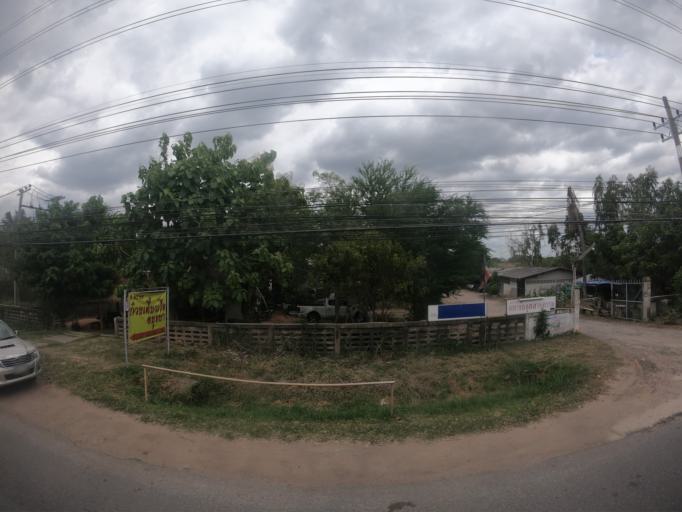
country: TH
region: Nakhon Ratchasima
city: Nakhon Ratchasima
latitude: 14.9455
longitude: 102.1279
